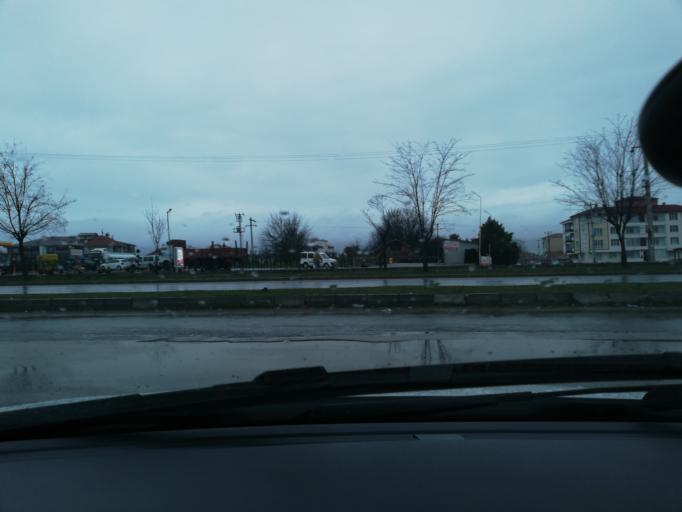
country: TR
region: Bolu
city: Bolu
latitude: 40.7359
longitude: 31.6298
